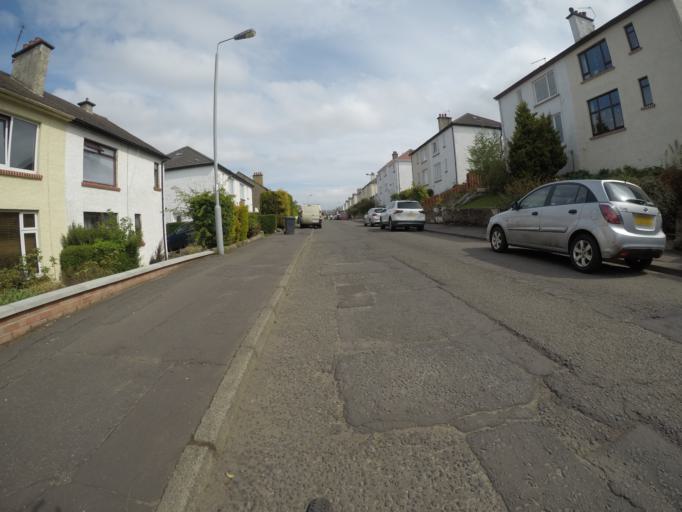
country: GB
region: Scotland
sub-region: East Renfrewshire
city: Giffnock
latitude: 55.8077
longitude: -4.2835
